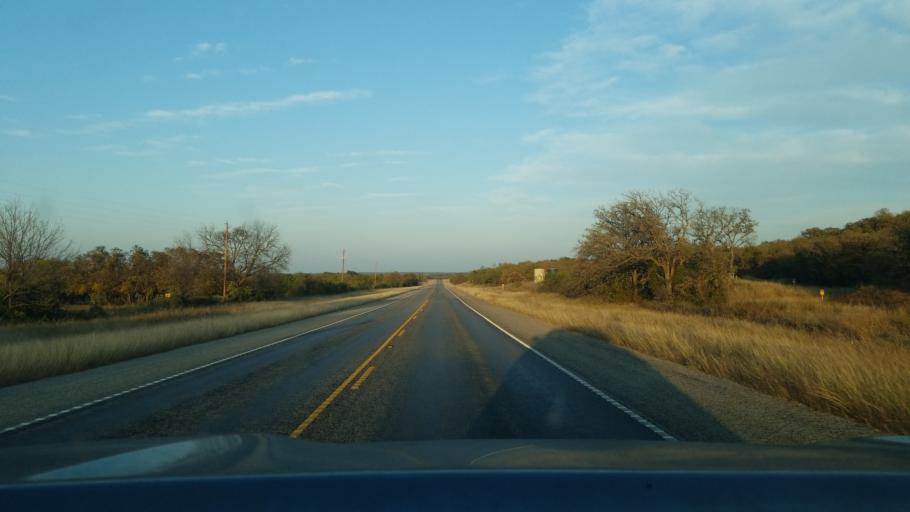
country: US
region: Texas
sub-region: Eastland County
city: Cisco
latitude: 32.4020
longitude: -98.9607
